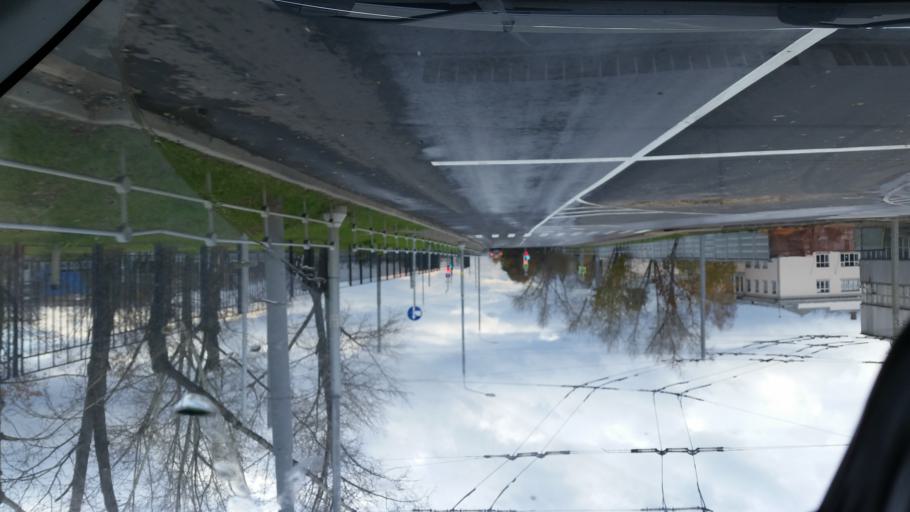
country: RU
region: Moscow
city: Kotlovka
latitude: 55.6722
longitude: 37.6219
